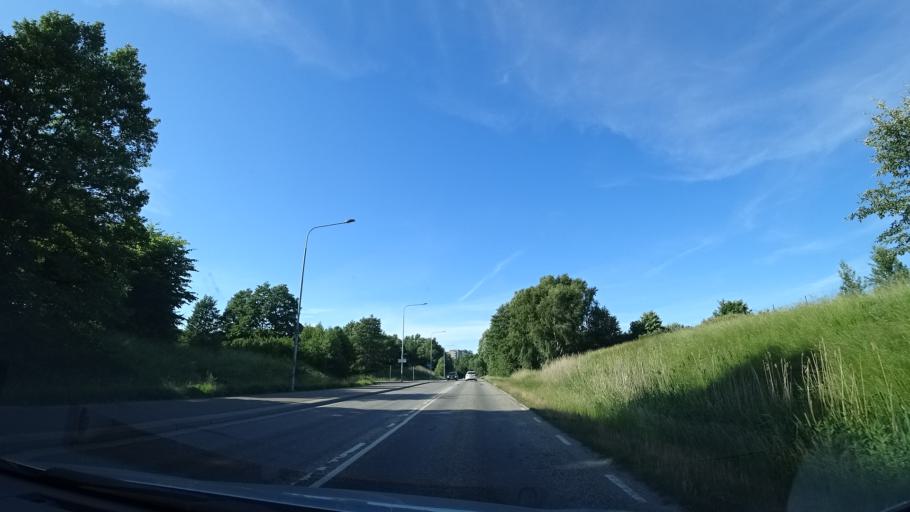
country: SE
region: Vaestra Goetaland
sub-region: Goteborg
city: Billdal
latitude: 57.5908
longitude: 11.9492
